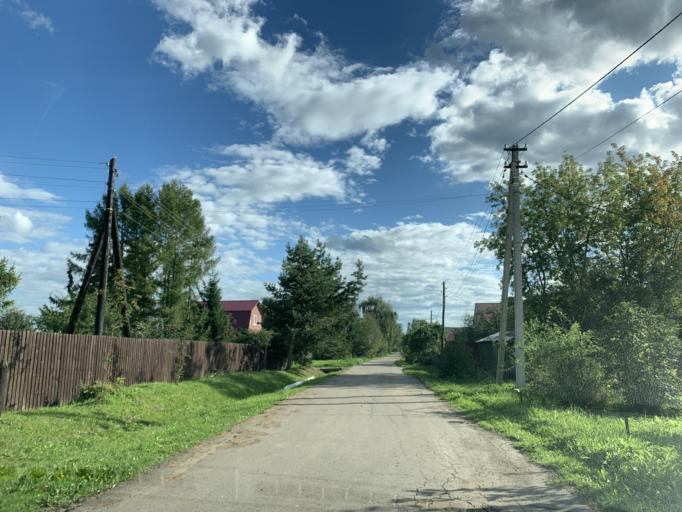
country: RU
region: Jaroslavl
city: Tunoshna
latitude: 57.6649
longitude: 40.0715
